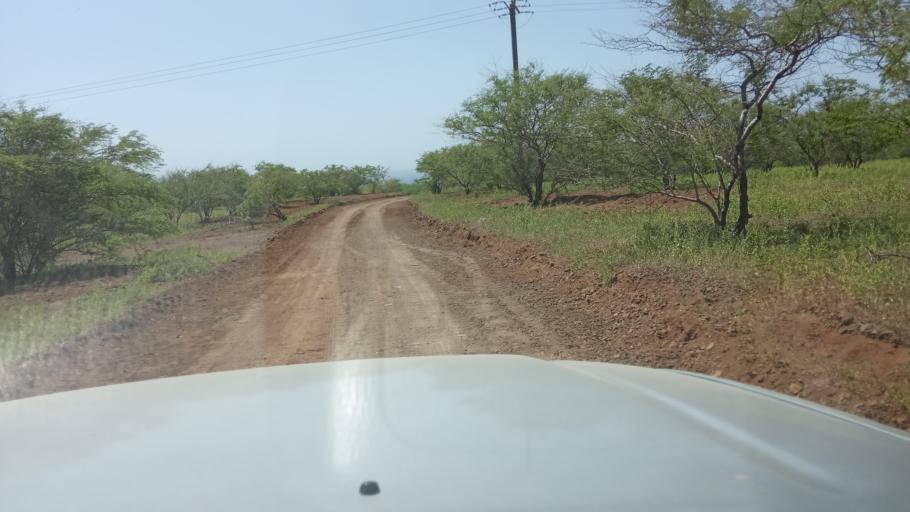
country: CV
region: Santa Catarina
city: Assomada
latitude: 15.1219
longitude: -23.7603
